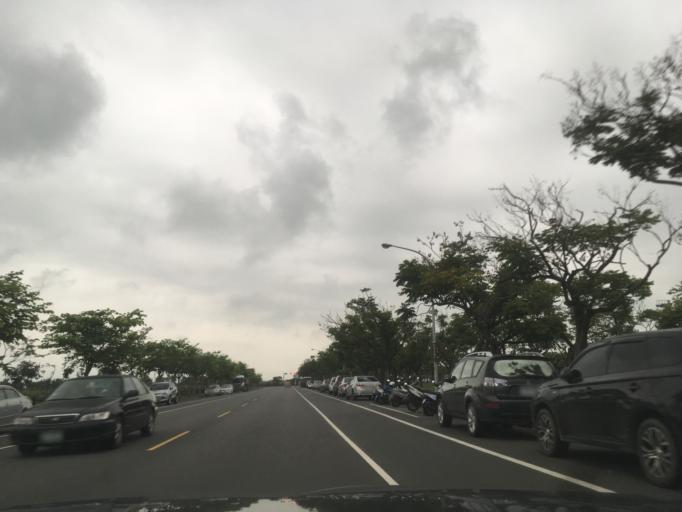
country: TW
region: Taiwan
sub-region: Yilan
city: Yilan
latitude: 24.7370
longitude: 121.7538
